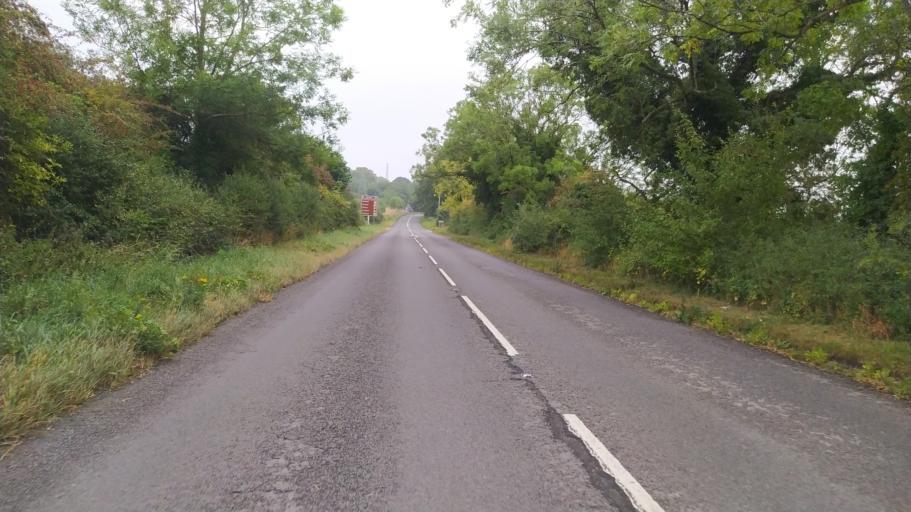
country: GB
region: England
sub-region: Wiltshire
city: Salisbury
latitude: 51.0517
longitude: -1.8164
